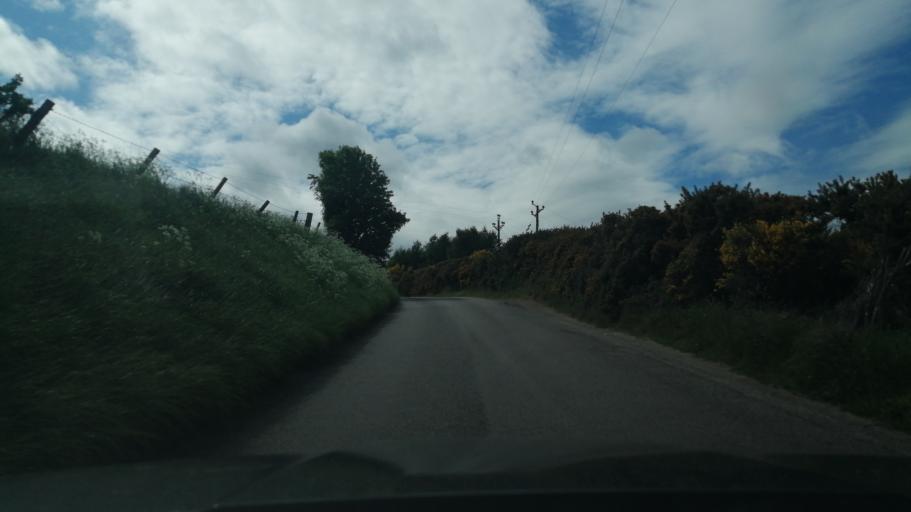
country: GB
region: Scotland
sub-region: Moray
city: Elgin
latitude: 57.6538
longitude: -3.2792
